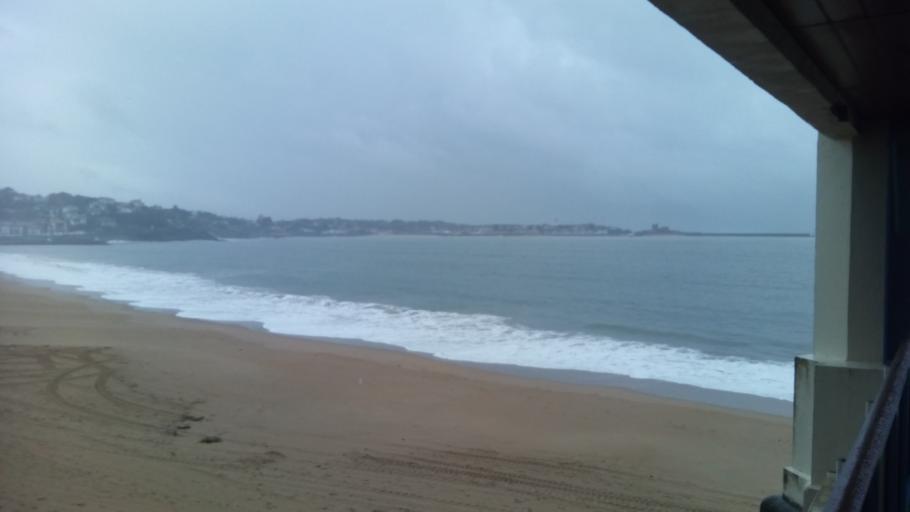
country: FR
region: Aquitaine
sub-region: Departement des Pyrenees-Atlantiques
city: Saint-Jean-de-Luz
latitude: 43.3914
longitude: -1.6612
